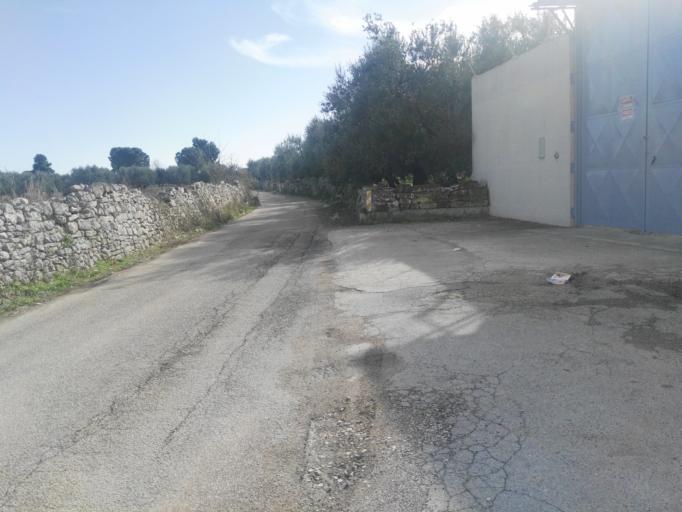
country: IT
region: Apulia
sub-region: Provincia di Barletta - Andria - Trani
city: Andria
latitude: 41.2159
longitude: 16.3058
